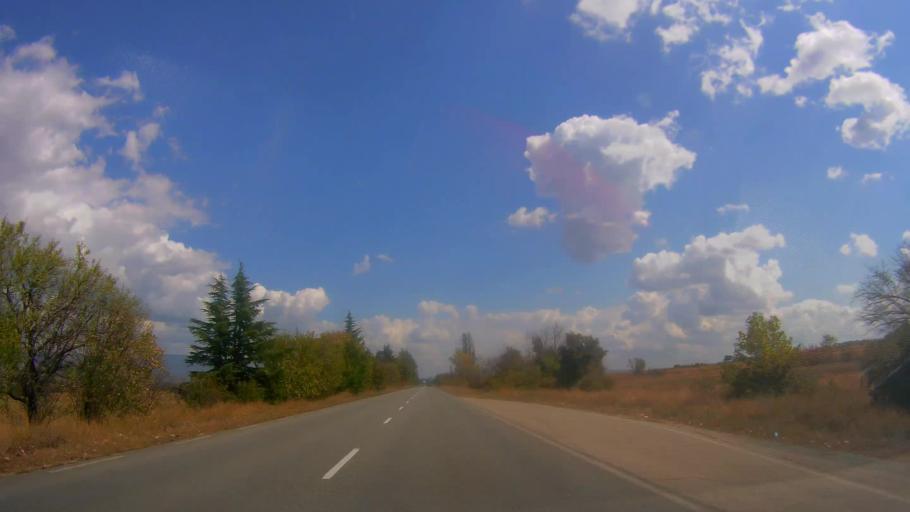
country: BG
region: Sliven
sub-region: Obshtina Tvurditsa
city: Tvurditsa
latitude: 42.6557
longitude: 25.9351
